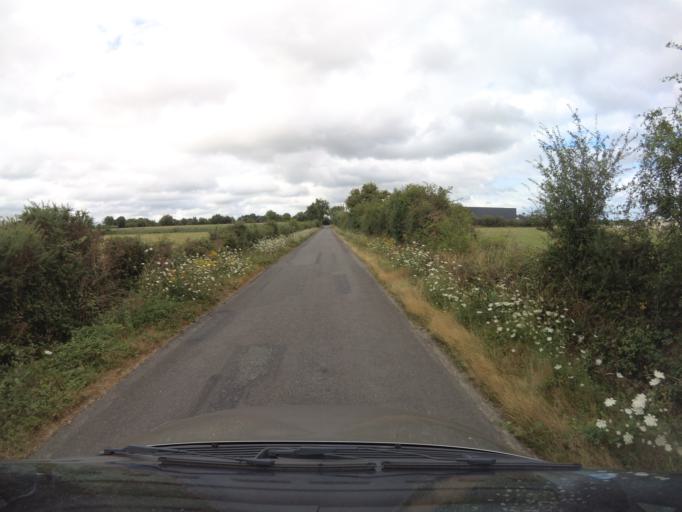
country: FR
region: Pays de la Loire
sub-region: Departement de la Vendee
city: Saint-Philbert-de-Bouaine
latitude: 46.9987
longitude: -1.5170
